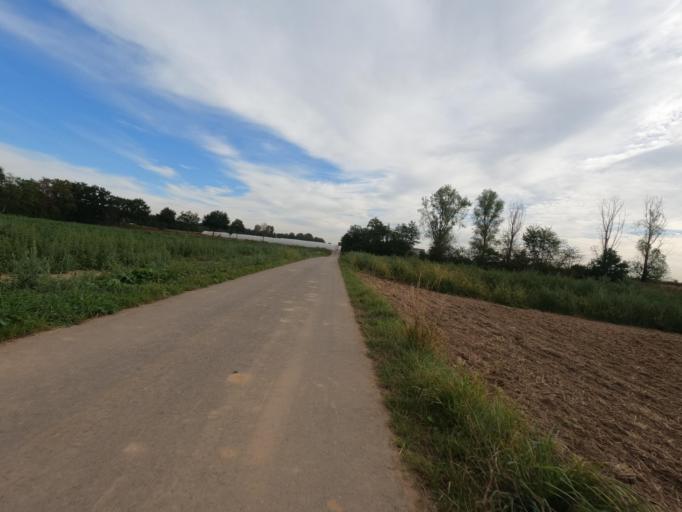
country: NL
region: Limburg
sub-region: Gemeente Roerdalen
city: Vlodrop
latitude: 51.1177
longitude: 6.0943
